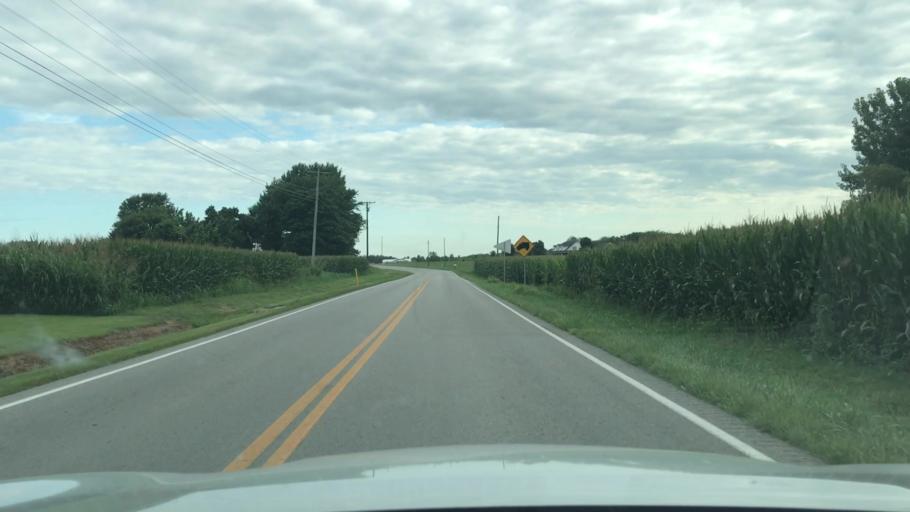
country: US
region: Kentucky
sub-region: Todd County
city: Elkton
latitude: 36.7799
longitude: -87.1639
